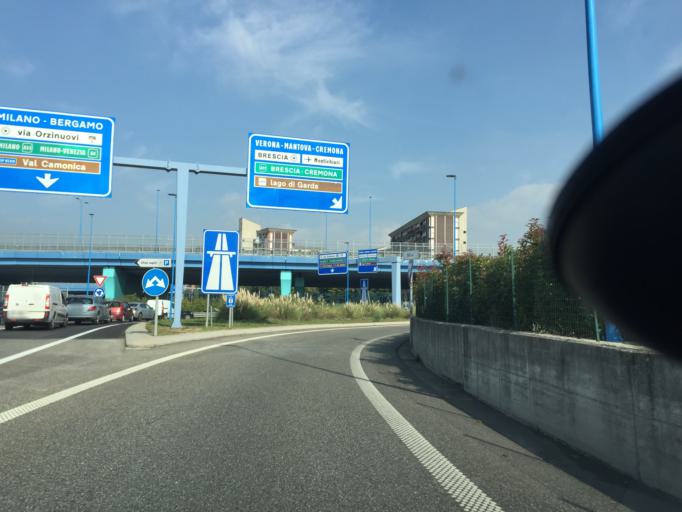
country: IT
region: Lombardy
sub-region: Provincia di Brescia
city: Roncadelle
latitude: 45.5247
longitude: 10.1749
